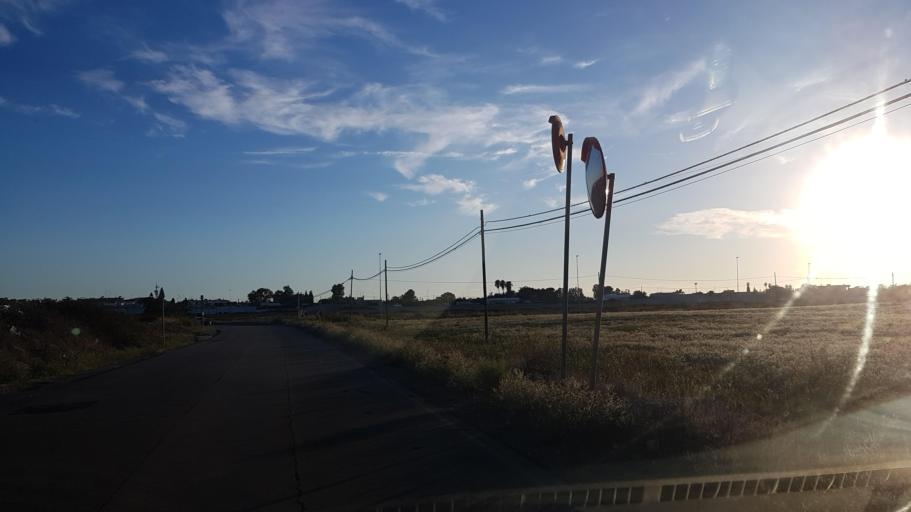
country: IT
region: Apulia
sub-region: Provincia di Lecce
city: Lecce
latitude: 40.3768
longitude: 18.1817
